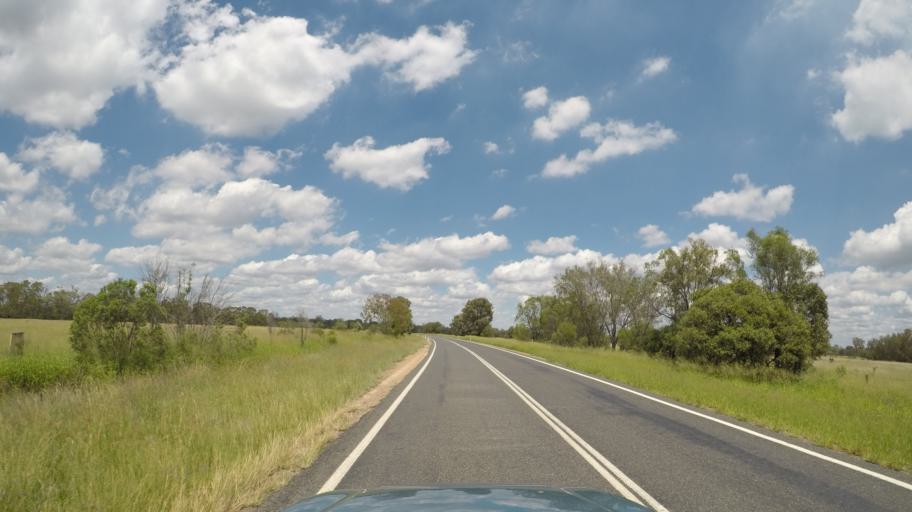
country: AU
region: Queensland
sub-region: Western Downs
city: Dalby
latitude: -27.9537
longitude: 151.1322
